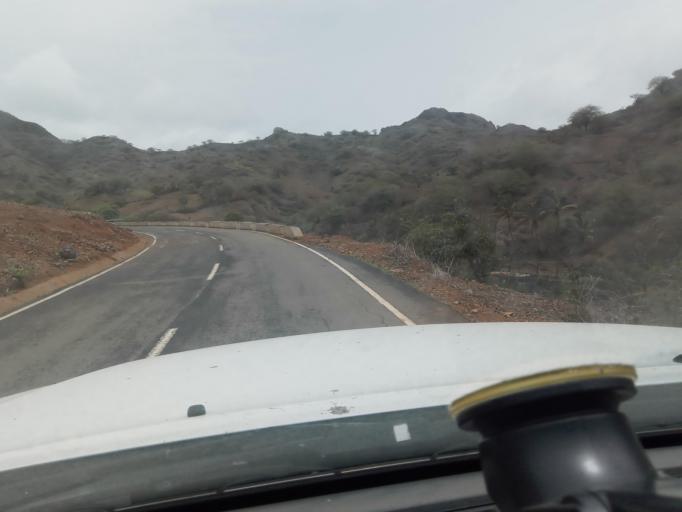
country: CV
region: Sao Miguel
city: Calheta
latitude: 15.1457
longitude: -23.6178
